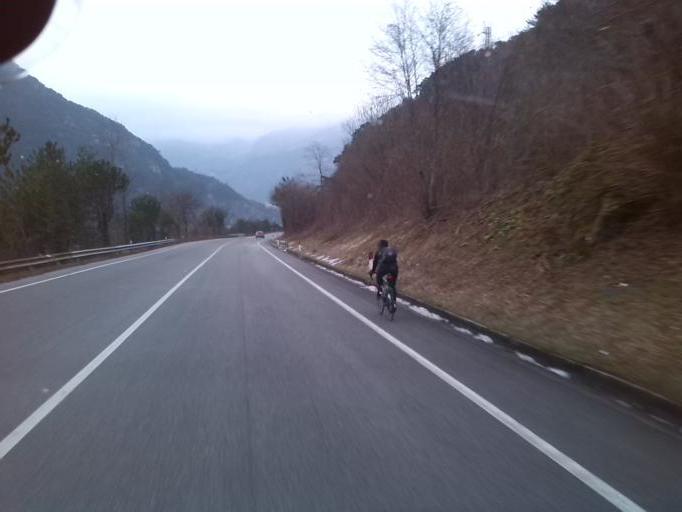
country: IT
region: Friuli Venezia Giulia
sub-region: Provincia di Udine
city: Moggio di Sotto
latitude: 46.3939
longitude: 13.1670
